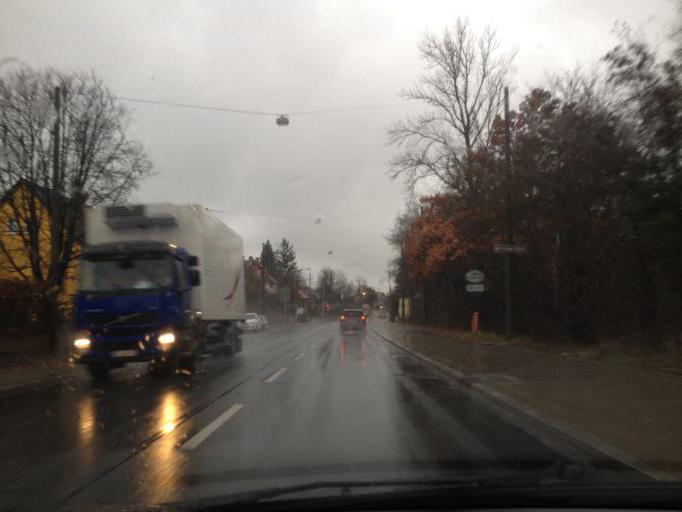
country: DE
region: Bavaria
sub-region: Regierungsbezirk Mittelfranken
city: Schwaig
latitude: 49.4675
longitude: 11.1584
